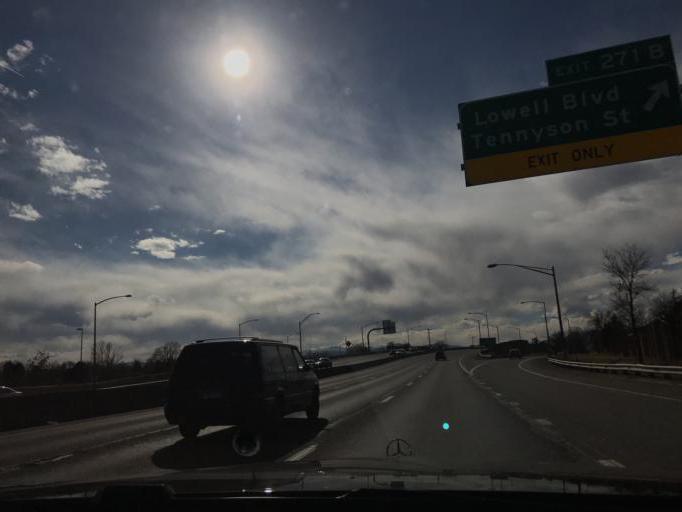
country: US
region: Colorado
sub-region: Adams County
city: Berkley
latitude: 39.7838
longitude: -105.0309
